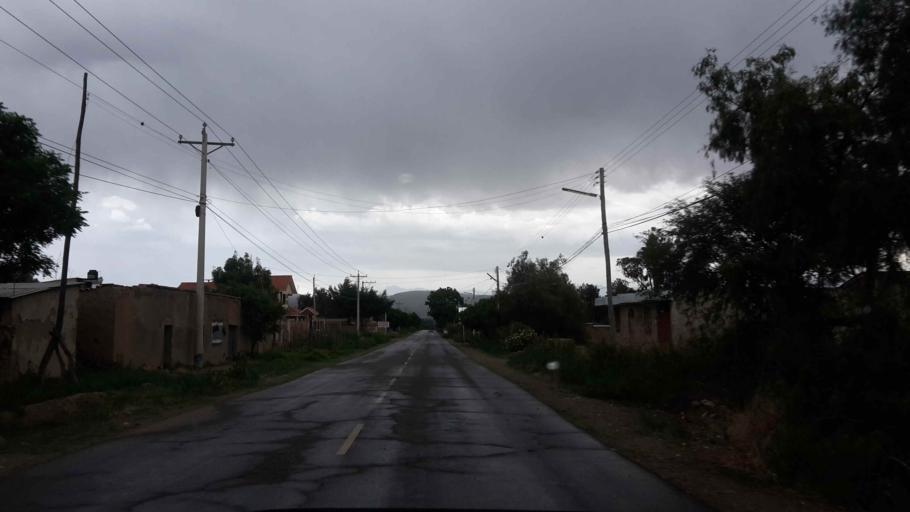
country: BO
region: Cochabamba
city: Tarata
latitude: -17.5776
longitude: -66.0595
